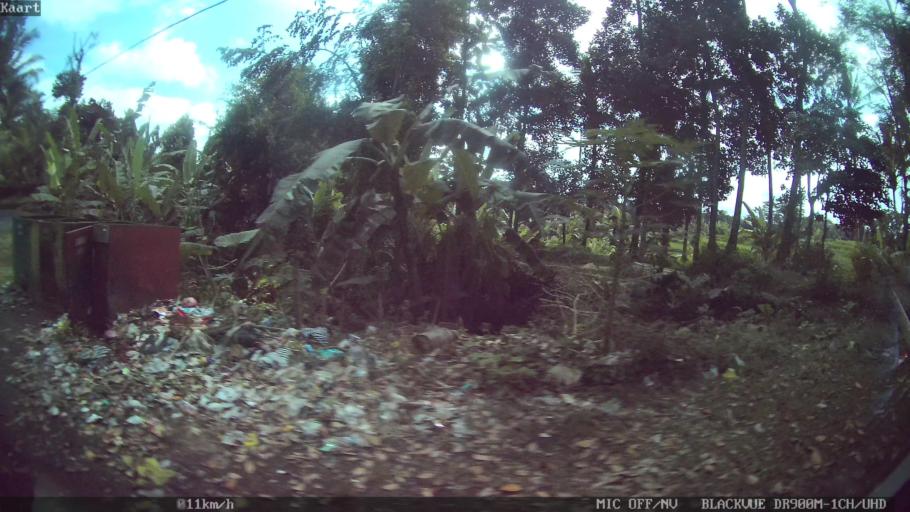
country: ID
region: Bali
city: Banjar Pesalakan
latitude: -8.5119
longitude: 115.3060
